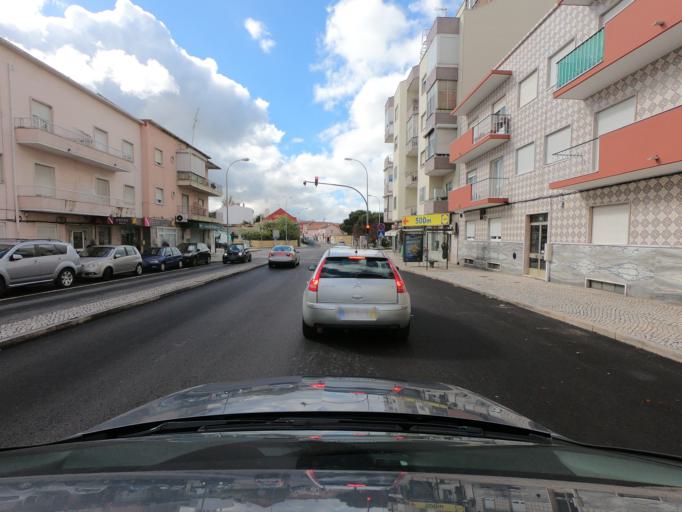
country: PT
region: Lisbon
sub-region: Oeiras
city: Linda-a-Velha
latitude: 38.7143
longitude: -9.2445
